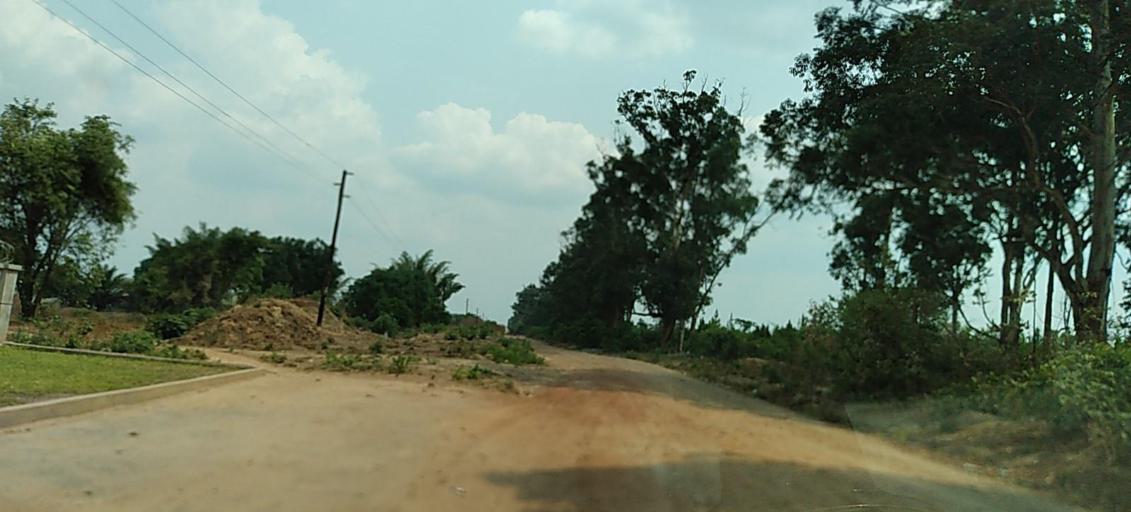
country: ZM
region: Copperbelt
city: Kalulushi
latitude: -12.8283
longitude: 28.0772
